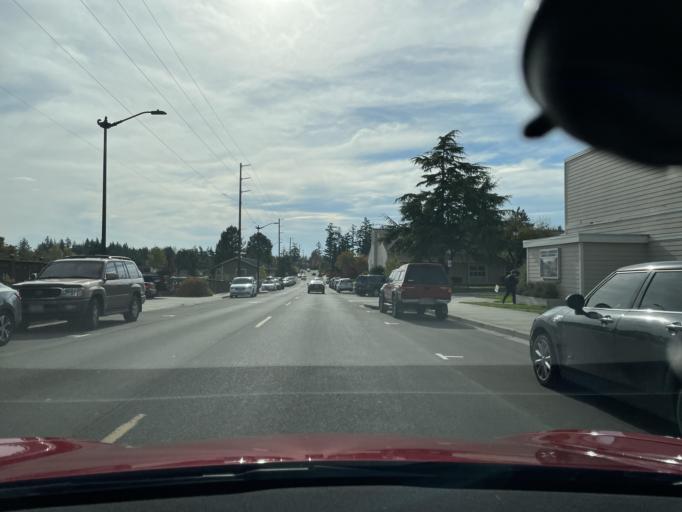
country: US
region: Washington
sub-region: San Juan County
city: Friday Harbor
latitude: 48.5360
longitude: -123.0204
